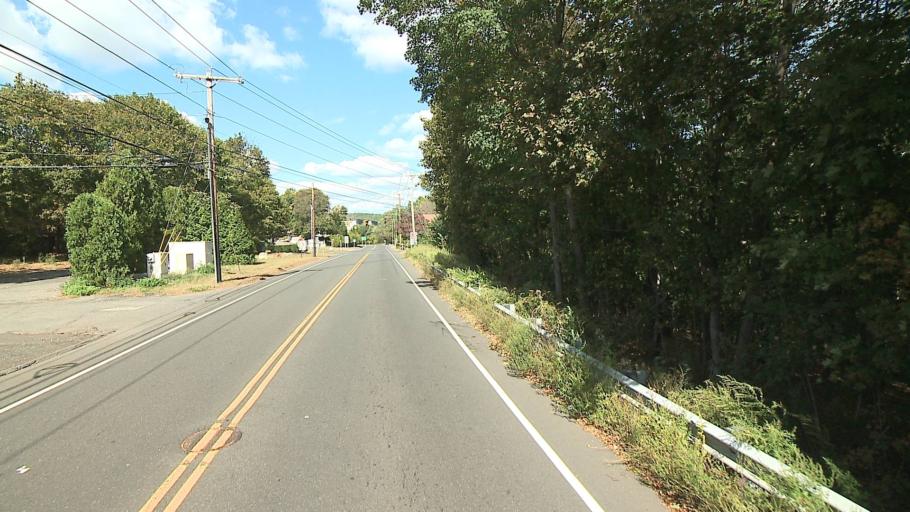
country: US
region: Connecticut
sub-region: New Haven County
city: Ansonia
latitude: 41.3560
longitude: -73.0913
